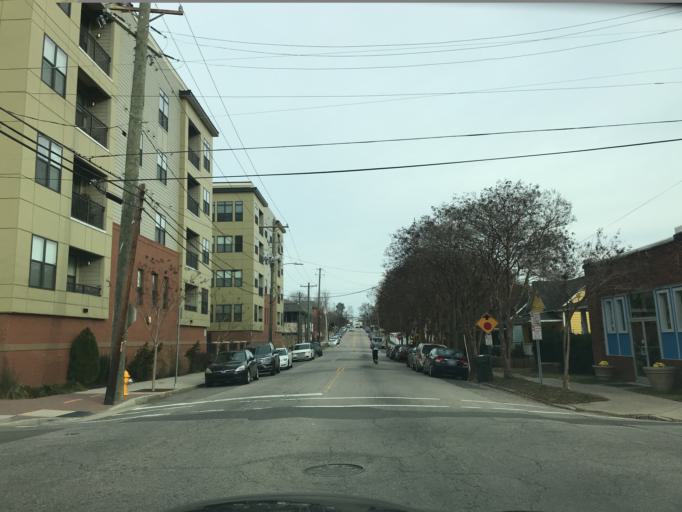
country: US
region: North Carolina
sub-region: Wake County
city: Raleigh
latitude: 35.7767
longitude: -78.6334
